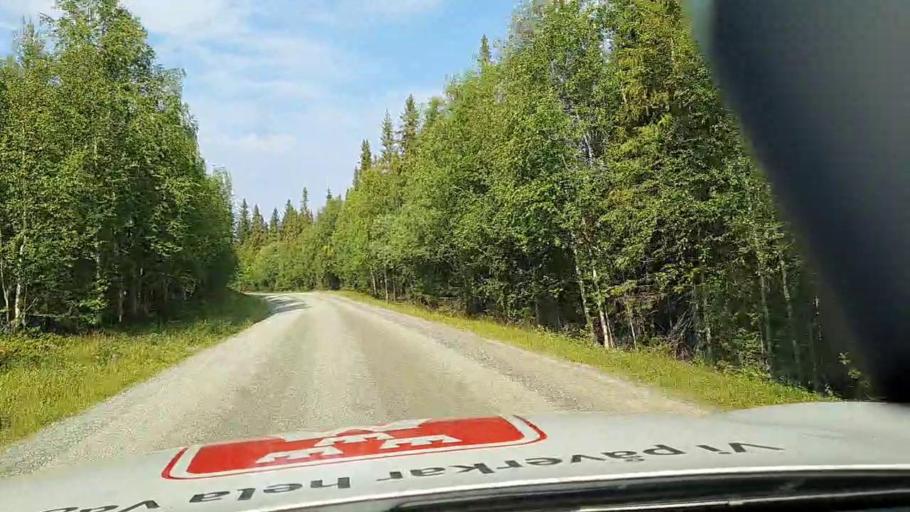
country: SE
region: Vaesterbotten
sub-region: Storumans Kommun
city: Fristad
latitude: 65.5376
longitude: 16.8086
